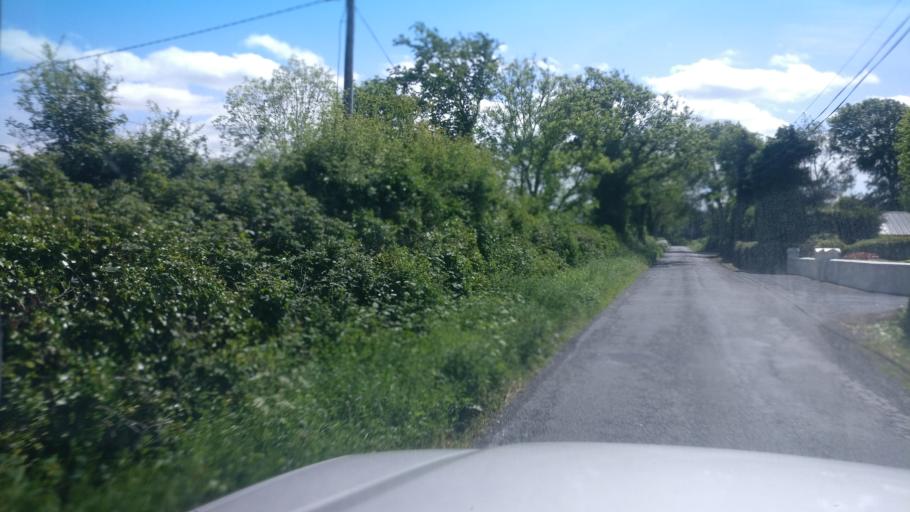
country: IE
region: Connaught
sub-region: County Galway
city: Gort
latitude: 53.1489
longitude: -8.7448
